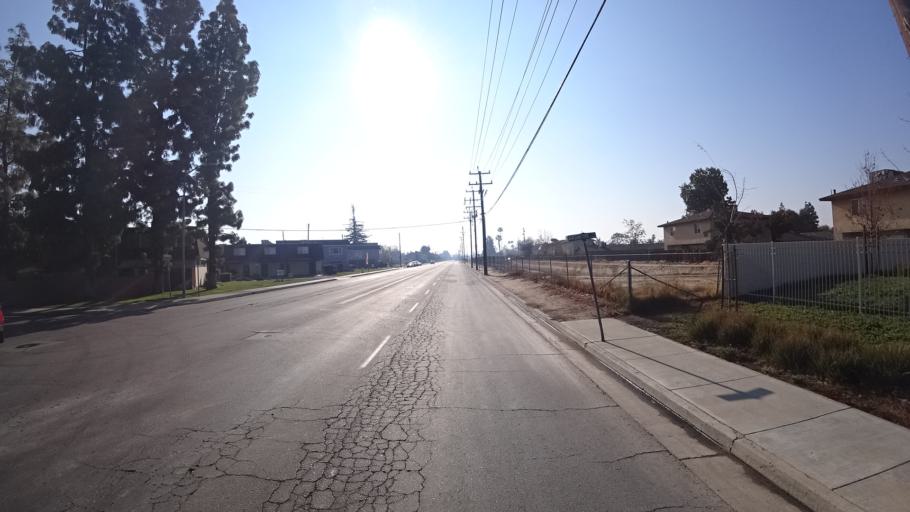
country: US
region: California
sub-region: Kern County
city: Bakersfield
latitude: 35.3378
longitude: -119.0518
